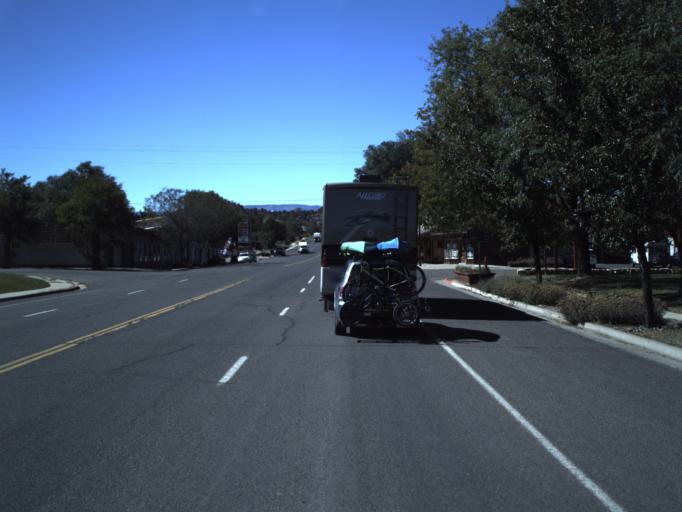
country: US
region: Utah
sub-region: Wayne County
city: Loa
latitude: 37.7704
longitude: -111.5995
